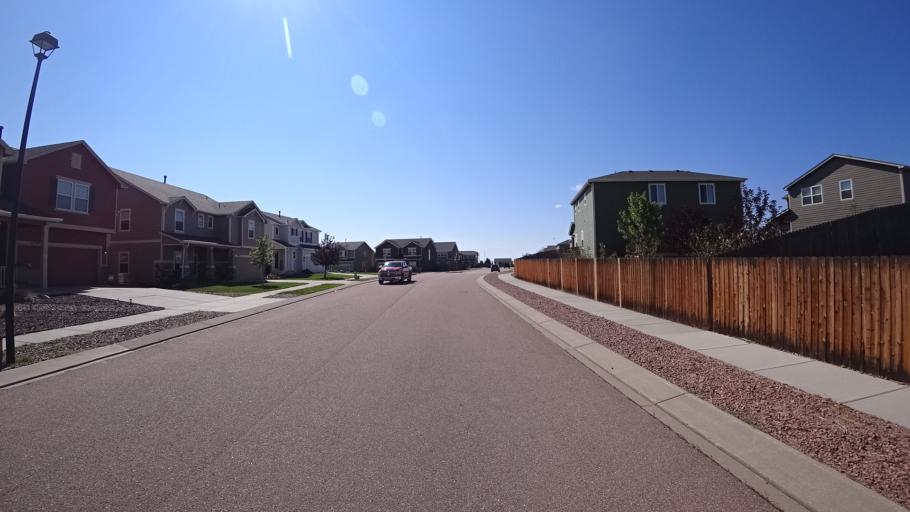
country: US
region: Colorado
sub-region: El Paso County
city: Cimarron Hills
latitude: 38.9279
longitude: -104.7073
